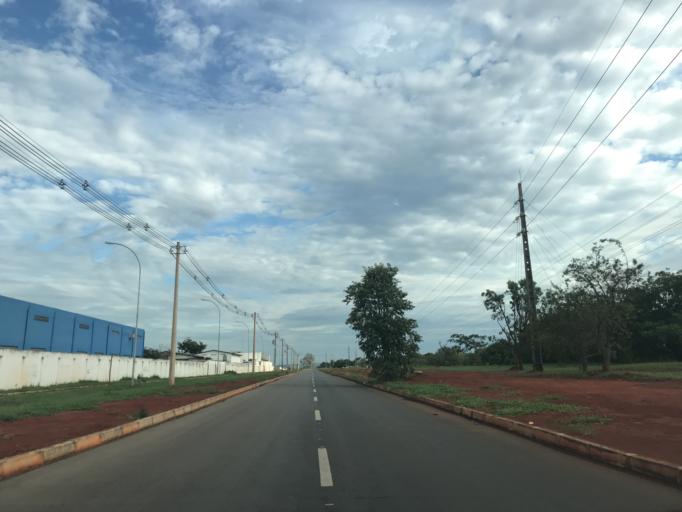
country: BR
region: Federal District
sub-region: Brasilia
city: Brasilia
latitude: -15.7796
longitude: -47.8948
